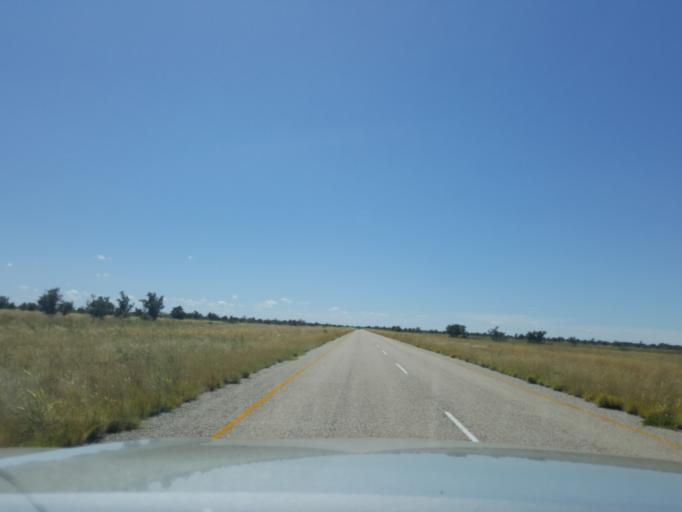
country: BW
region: Central
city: Gweta
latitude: -20.2179
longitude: 25.0703
